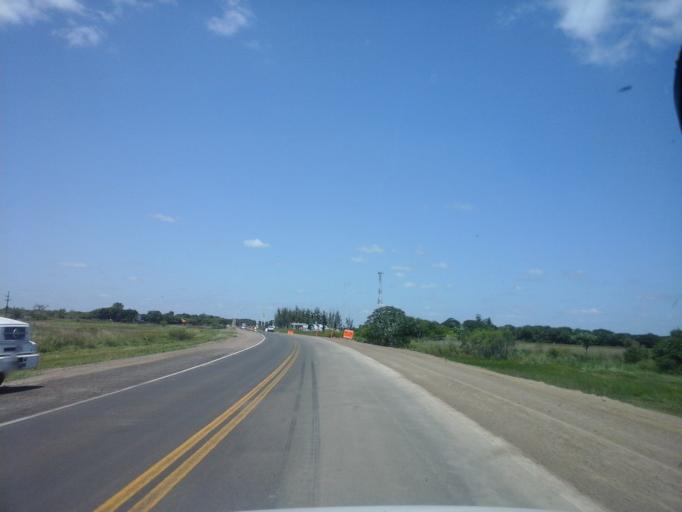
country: AR
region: Corrientes
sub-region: Departamento de Itati
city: Itati
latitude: -27.3495
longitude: -58.2349
